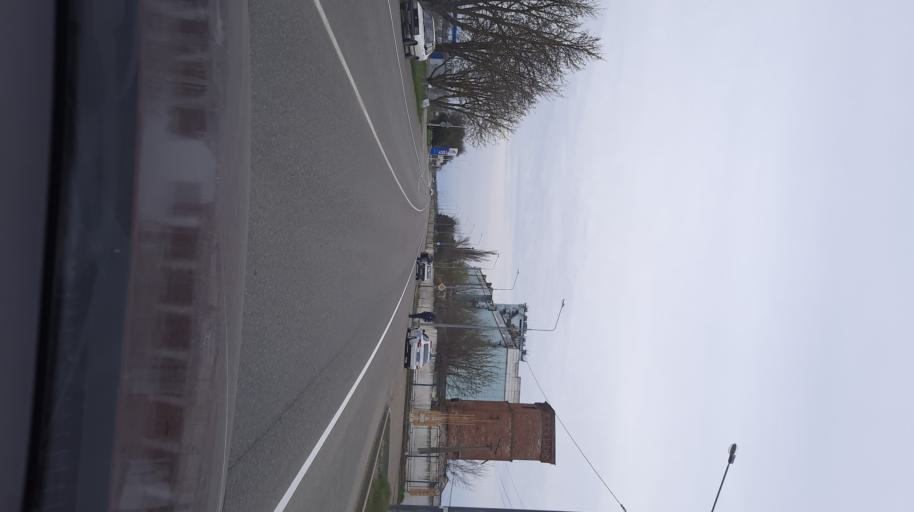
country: RU
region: Krasnodarskiy
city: Ol'ginskaya
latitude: 45.9301
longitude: 38.5266
